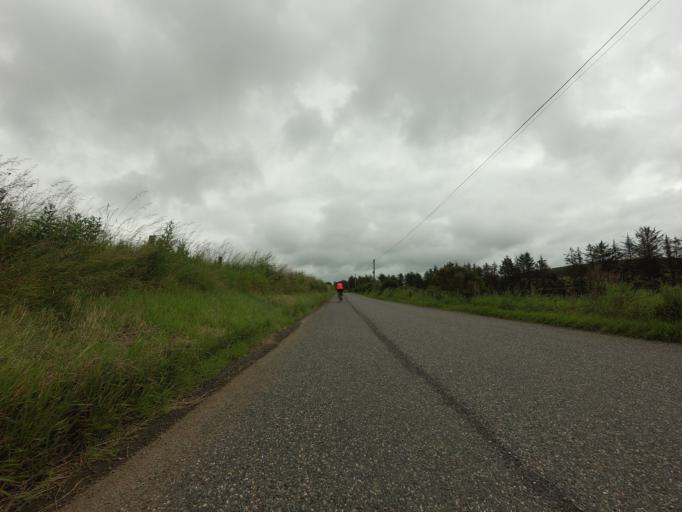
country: GB
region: Scotland
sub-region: Aberdeenshire
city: Turriff
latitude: 57.5347
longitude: -2.3755
